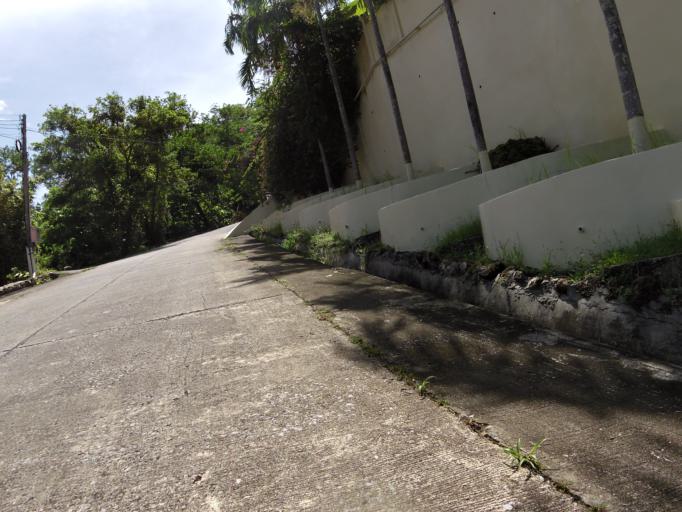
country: TH
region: Phuket
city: Ban Karon
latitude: 7.8471
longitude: 98.3015
